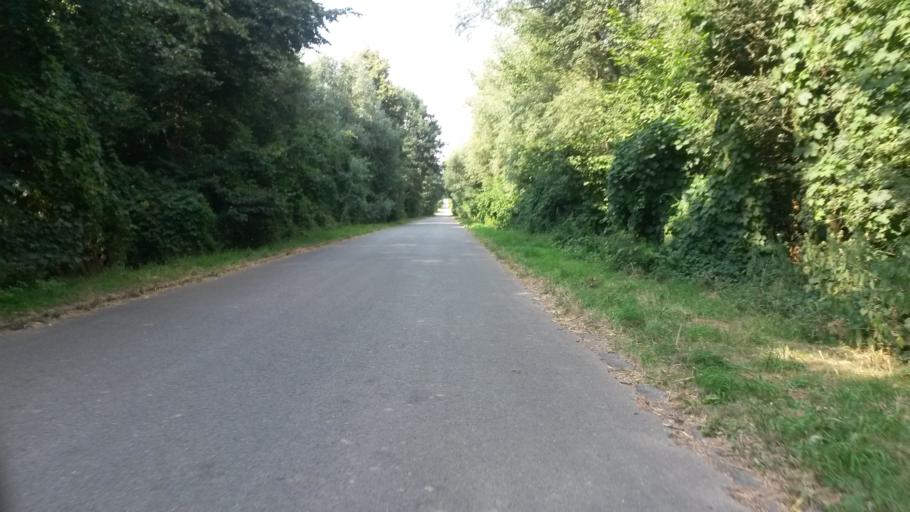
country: DE
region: Lower Saxony
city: Riede
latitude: 53.0290
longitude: 8.9327
